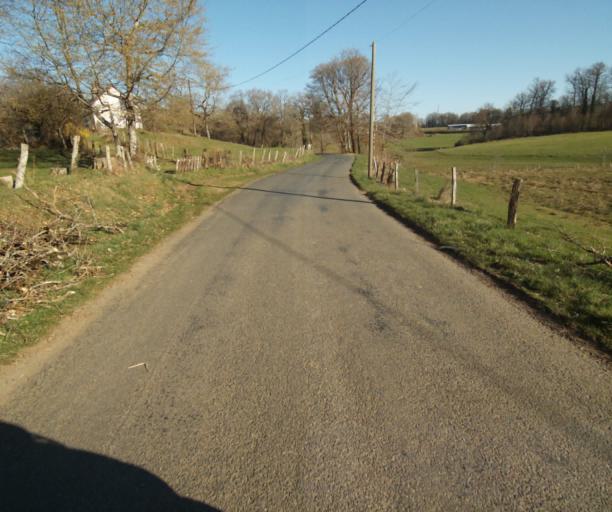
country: FR
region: Limousin
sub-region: Departement de la Correze
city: Saint-Clement
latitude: 45.3801
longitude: 1.6431
